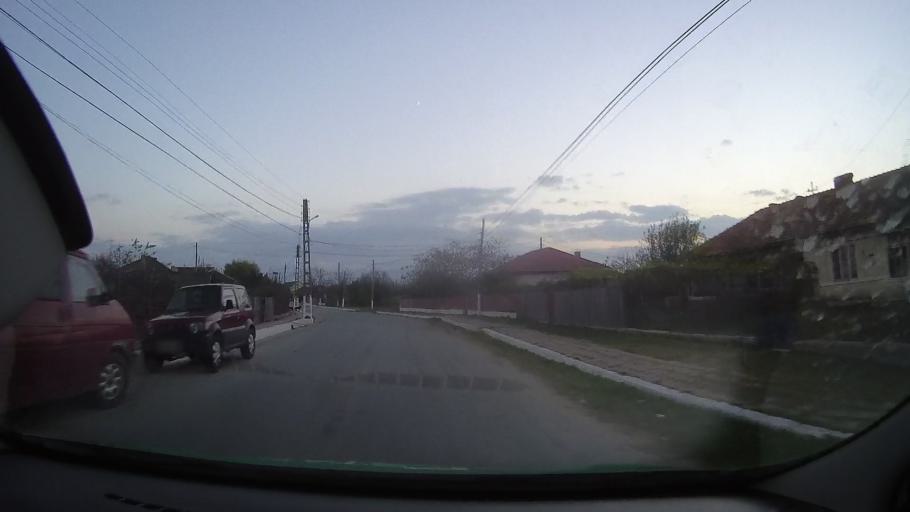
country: RO
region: Constanta
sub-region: Comuna Oltina
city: Oltina
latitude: 44.1674
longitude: 27.6649
